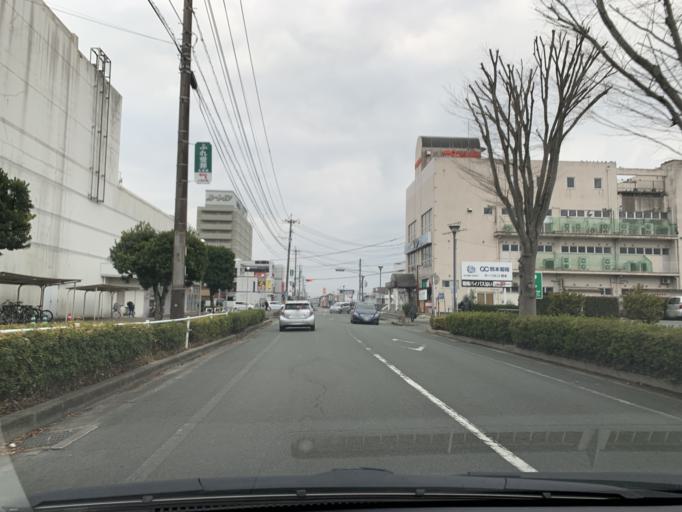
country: JP
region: Kumamoto
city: Ozu
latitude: 32.8765
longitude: 130.8666
